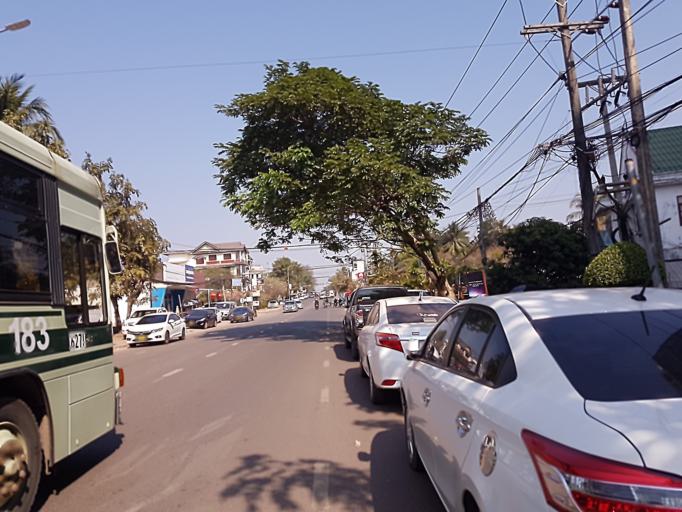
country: LA
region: Vientiane
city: Vientiane
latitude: 17.9738
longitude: 102.6282
